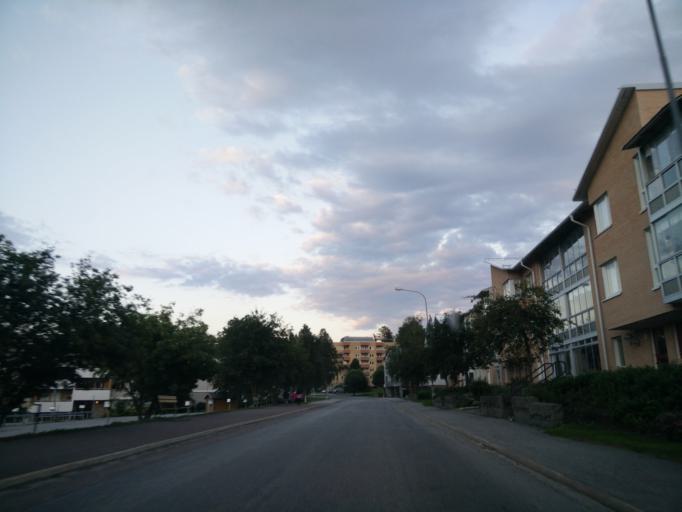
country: SE
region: Vaesternorrland
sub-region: Solleftea Kommun
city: Solleftea
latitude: 63.1673
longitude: 17.2773
